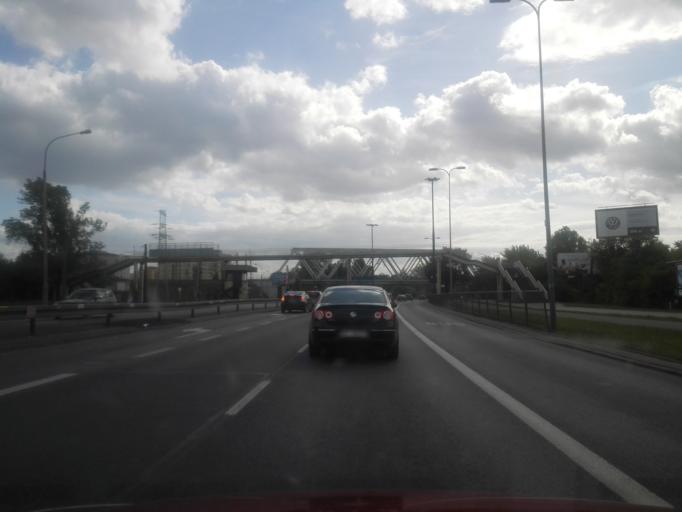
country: PL
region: Masovian Voivodeship
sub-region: Warszawa
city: Praga Polnoc
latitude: 52.2649
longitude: 21.0570
